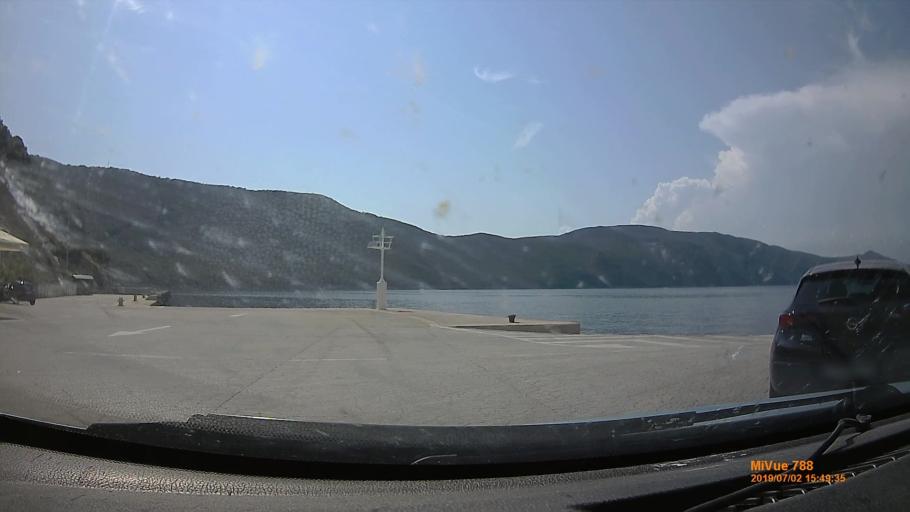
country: HR
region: Primorsko-Goranska
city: Cres
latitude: 44.9798
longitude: 14.4485
